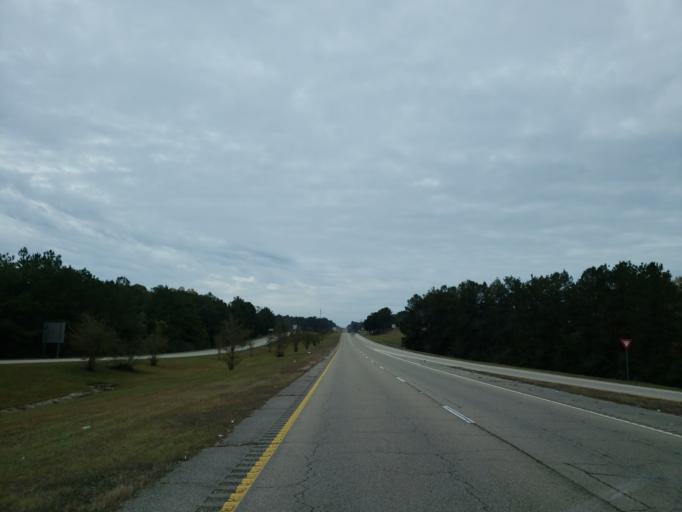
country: US
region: Mississippi
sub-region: Forrest County
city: Hattiesburg
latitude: 31.2408
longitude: -89.2744
